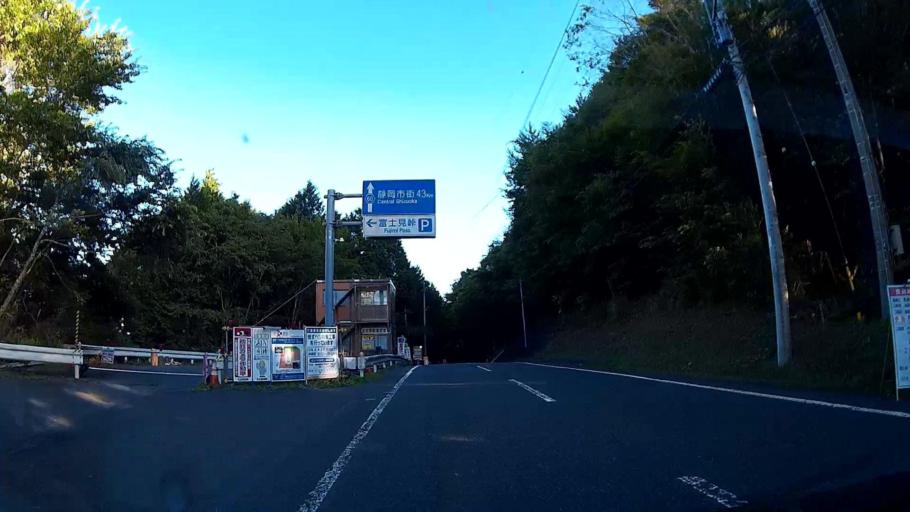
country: JP
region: Shizuoka
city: Shizuoka-shi
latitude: 35.1859
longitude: 138.2497
